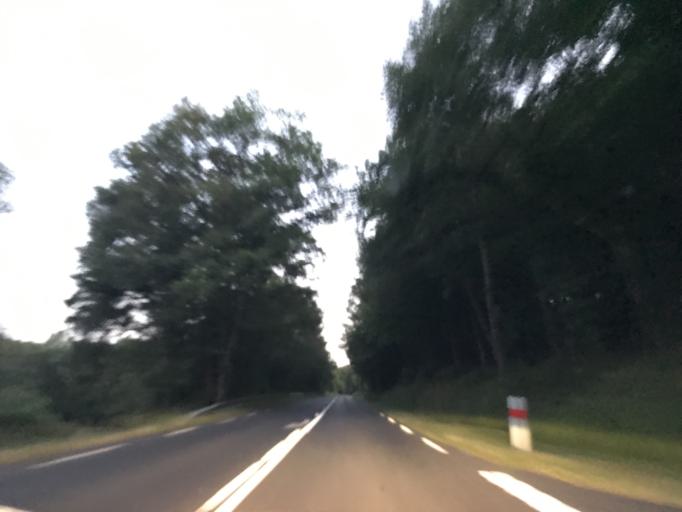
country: FR
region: Auvergne
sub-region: Departement du Puy-de-Dome
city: Orleat
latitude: 45.8280
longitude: 3.4550
